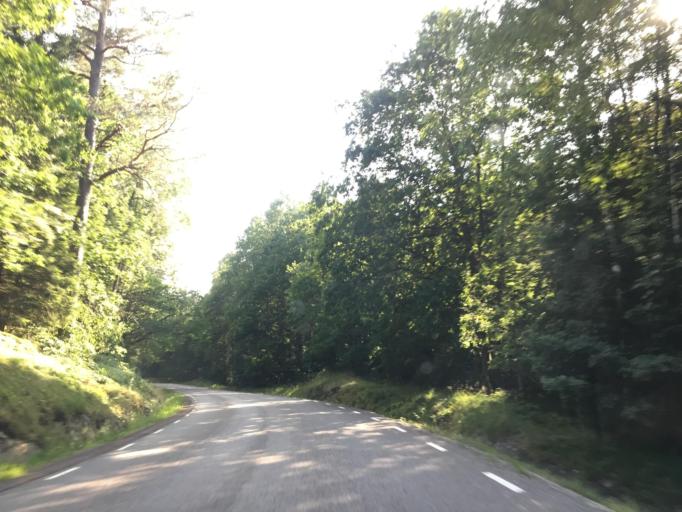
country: SE
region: Vaestra Goetaland
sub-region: Trollhattan
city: Trollhattan
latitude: 58.2655
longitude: 12.2344
